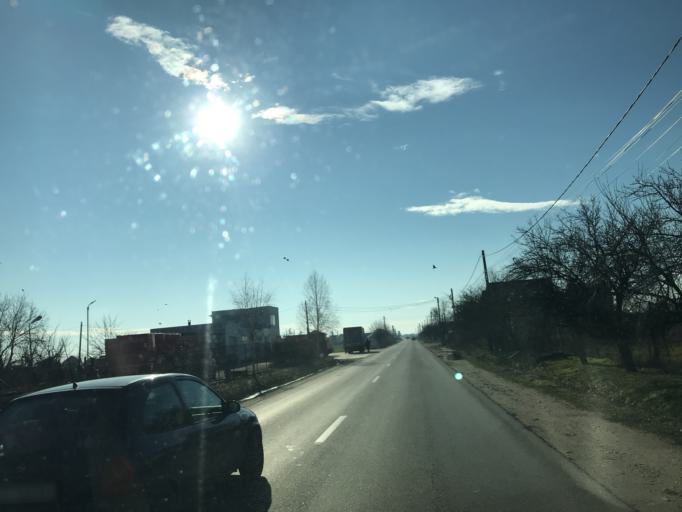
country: RO
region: Olt
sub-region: Comuna Slatioara
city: Slatioara
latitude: 44.3964
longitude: 24.3251
